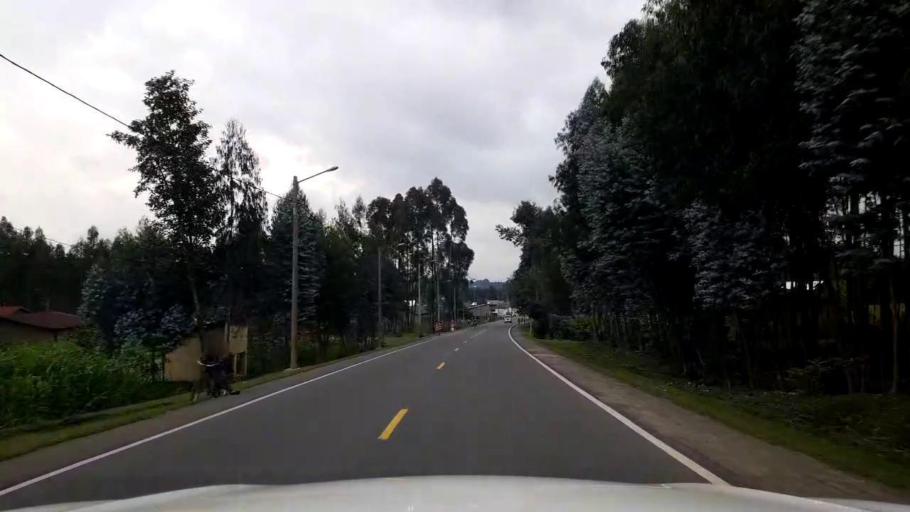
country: RW
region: Northern Province
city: Musanze
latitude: -1.5742
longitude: 29.5316
